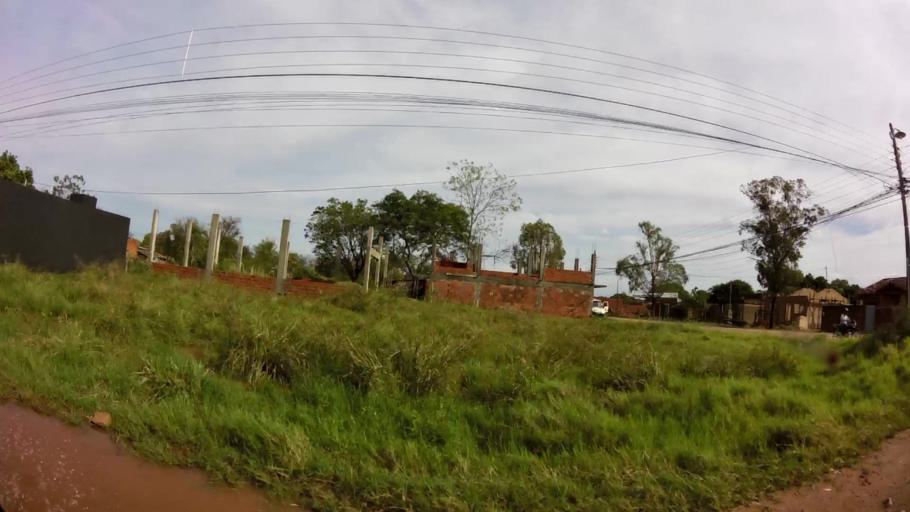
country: PY
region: Central
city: Limpio
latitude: -25.1767
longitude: -57.4940
